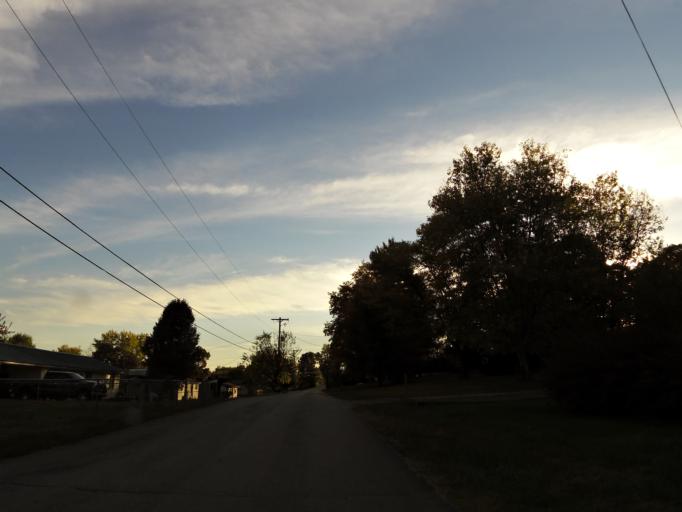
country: US
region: Tennessee
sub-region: Blount County
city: Eagleton Village
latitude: 35.7894
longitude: -83.9500
